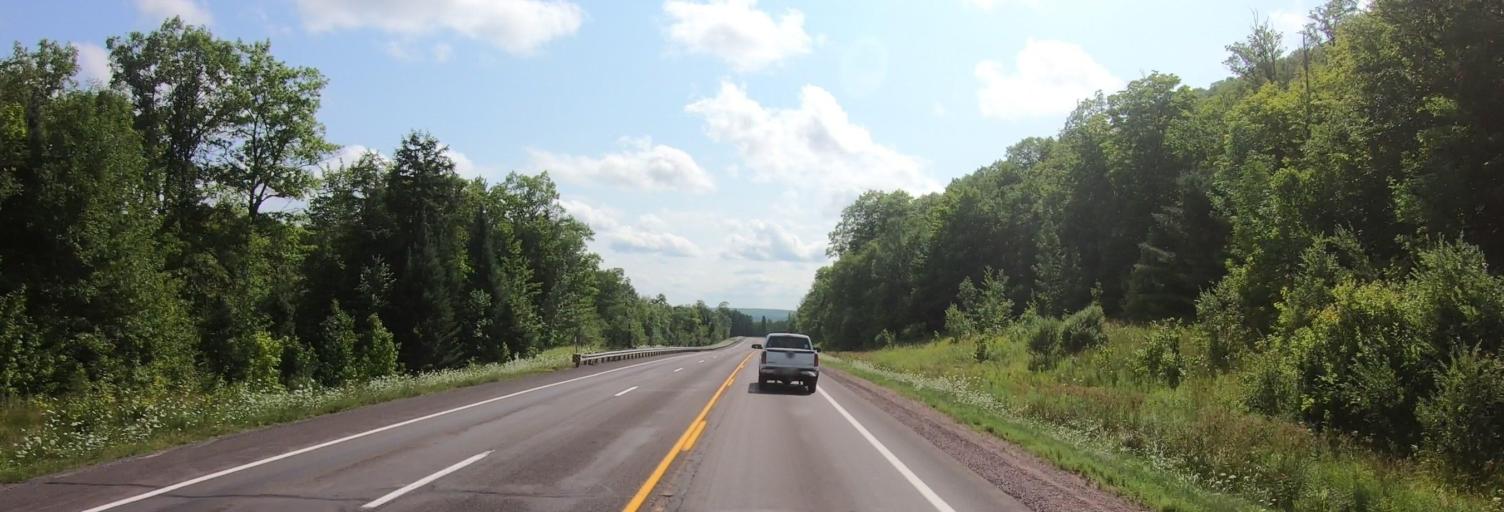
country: US
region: Michigan
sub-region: Ontonagon County
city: Ontonagon
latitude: 46.8062
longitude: -88.9987
